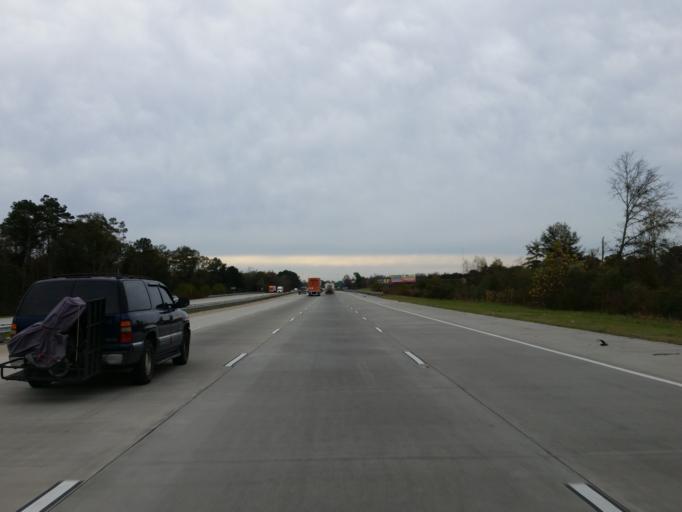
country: US
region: Georgia
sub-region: Dooly County
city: Unadilla
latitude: 32.2072
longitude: -83.7463
